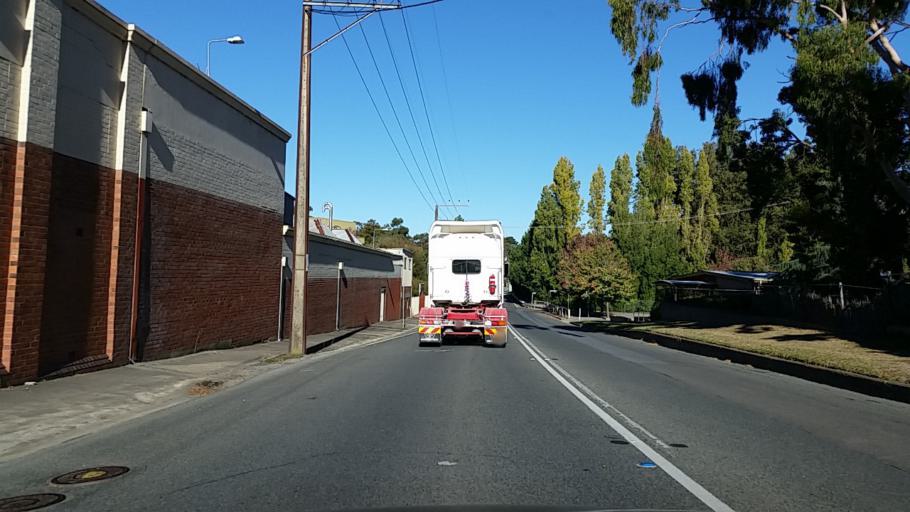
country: AU
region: South Australia
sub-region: Mount Barker
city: Nairne
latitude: -35.0377
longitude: 138.9171
